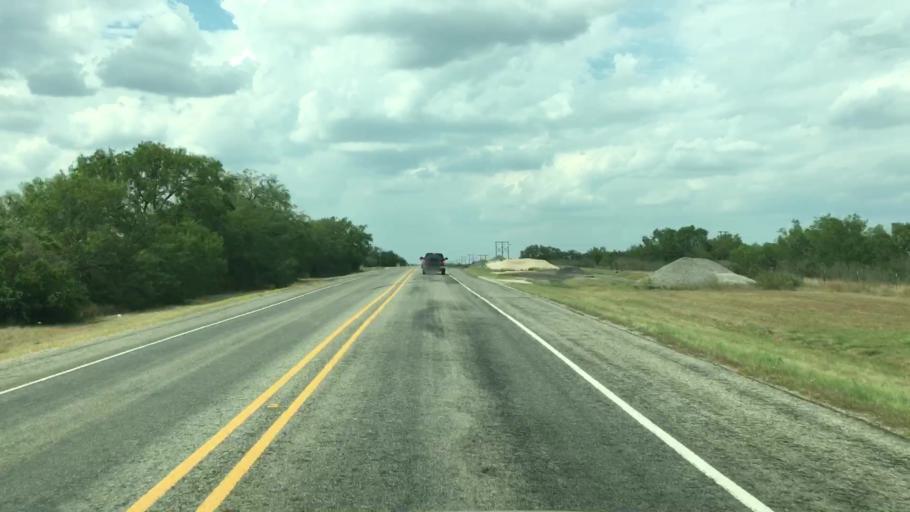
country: US
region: Texas
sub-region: Live Oak County
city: Three Rivers
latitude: 28.6452
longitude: -98.2845
